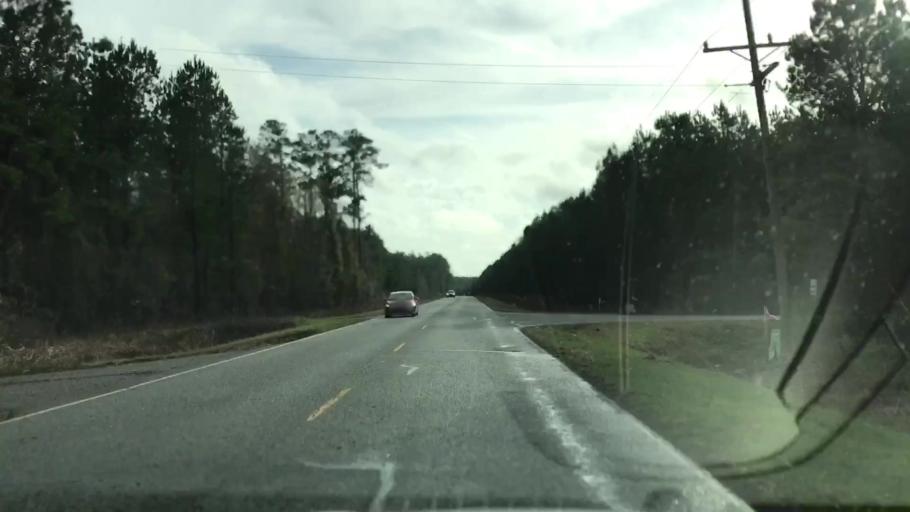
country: US
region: South Carolina
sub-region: Williamsburg County
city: Andrews
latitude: 33.4292
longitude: -79.5942
